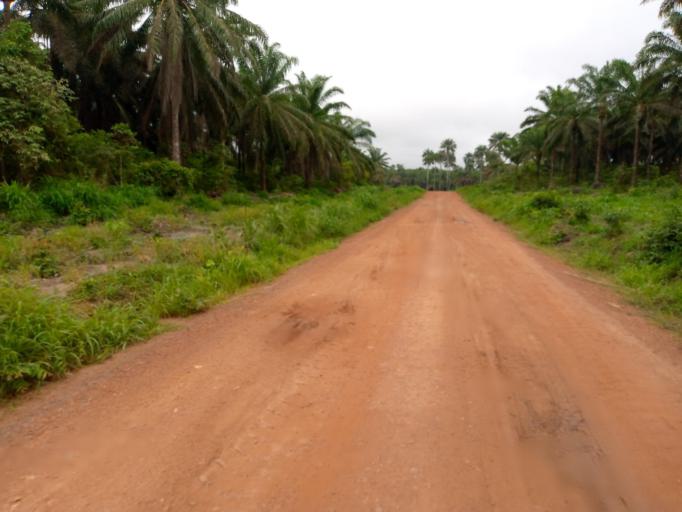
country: SL
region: Southern Province
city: Sumbuya
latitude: 7.5727
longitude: -12.0880
